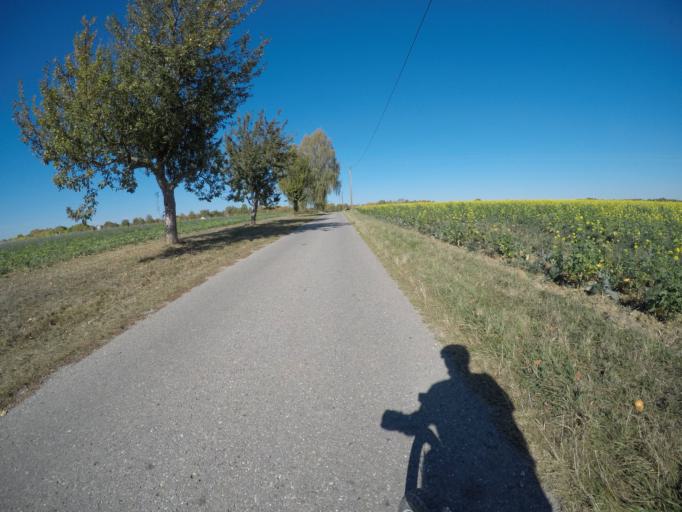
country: DE
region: Baden-Wuerttemberg
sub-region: Regierungsbezirk Stuttgart
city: Bondorf
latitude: 48.5355
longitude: 8.8615
